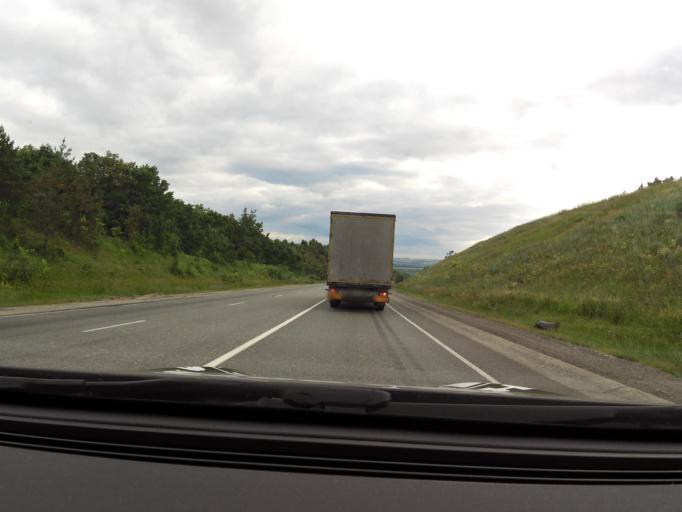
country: RU
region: Tatarstan
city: Sviyazhsk
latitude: 55.7223
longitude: 48.7467
